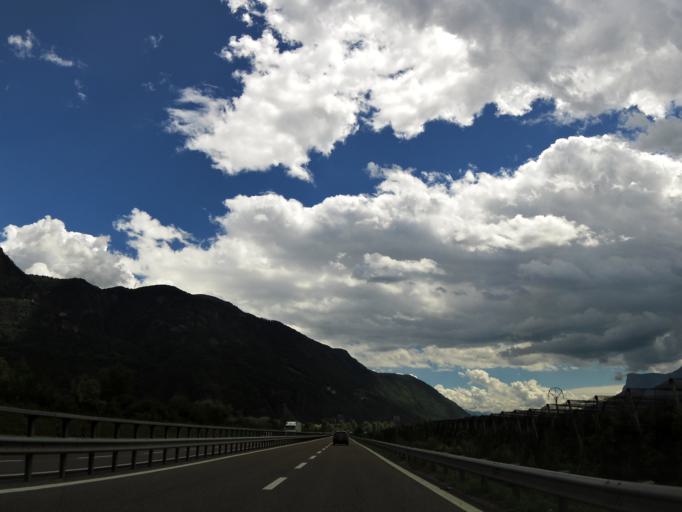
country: IT
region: Trentino-Alto Adige
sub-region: Bolzano
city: Sinigo
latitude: 46.6427
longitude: 11.1645
